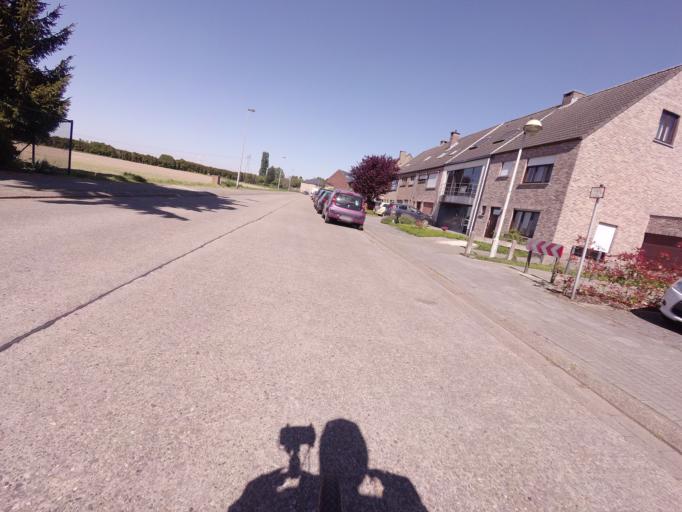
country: BE
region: Flanders
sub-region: Provincie Antwerpen
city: Boechout
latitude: 51.1701
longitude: 4.4972
